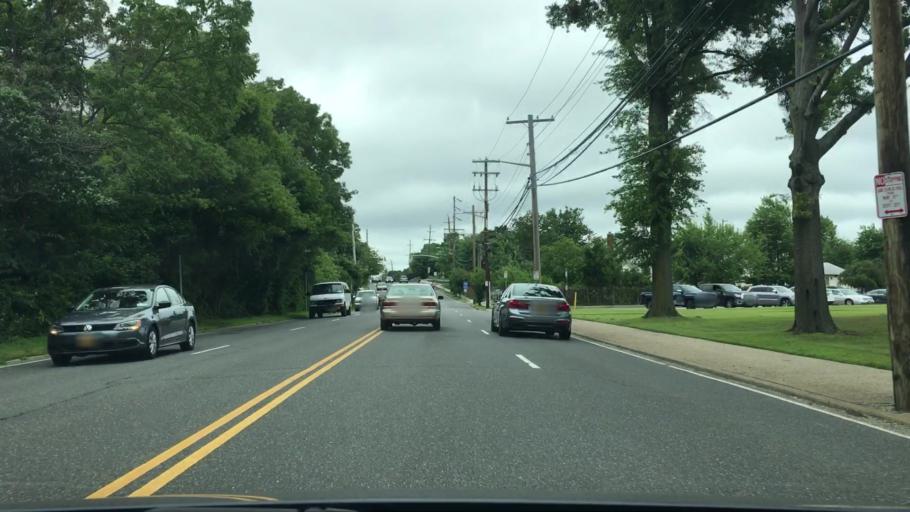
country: US
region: New York
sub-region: Nassau County
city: North Valley Stream
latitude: 40.6808
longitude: -73.6895
